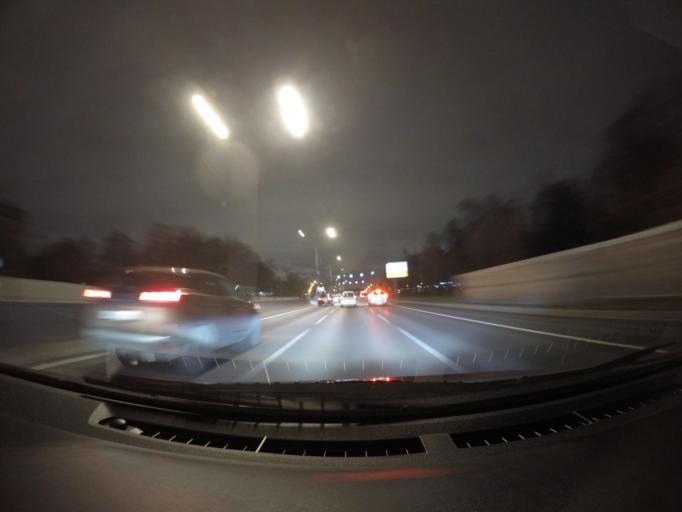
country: RU
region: Moscow
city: Kuz'minki
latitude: 55.6996
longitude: 37.7993
